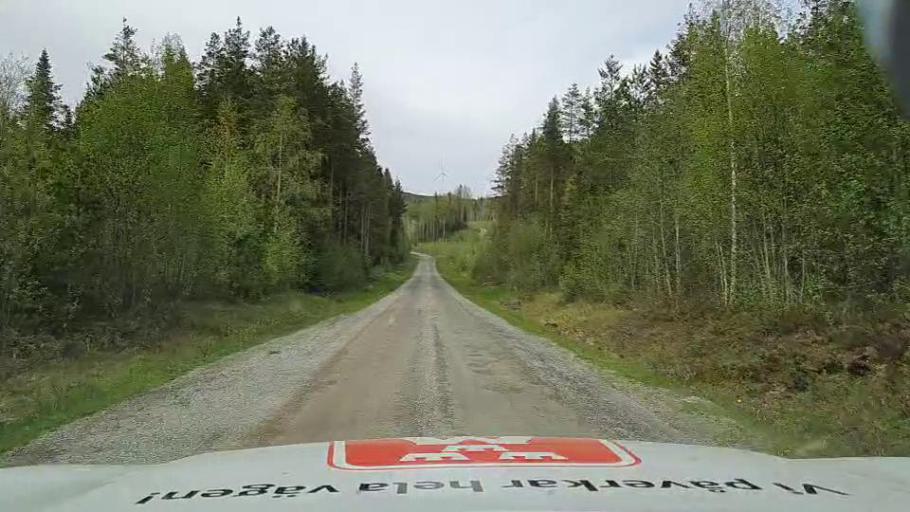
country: SE
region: Jaemtland
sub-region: Bergs Kommun
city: Hoverberg
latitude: 62.5255
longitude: 14.9145
